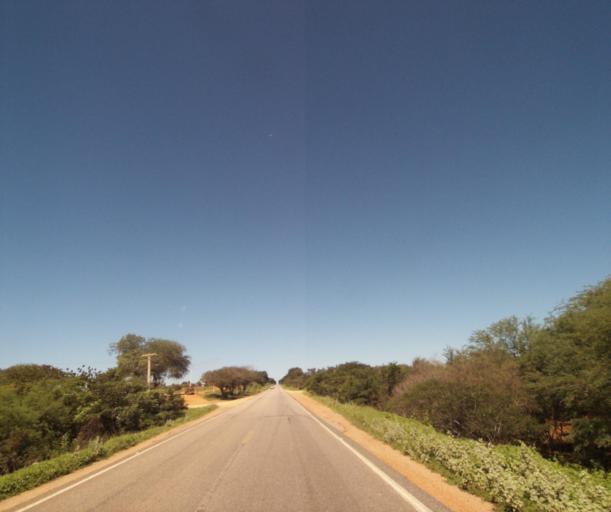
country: BR
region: Bahia
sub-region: Palmas De Monte Alto
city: Palmas de Monte Alto
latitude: -14.2601
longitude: -43.2932
